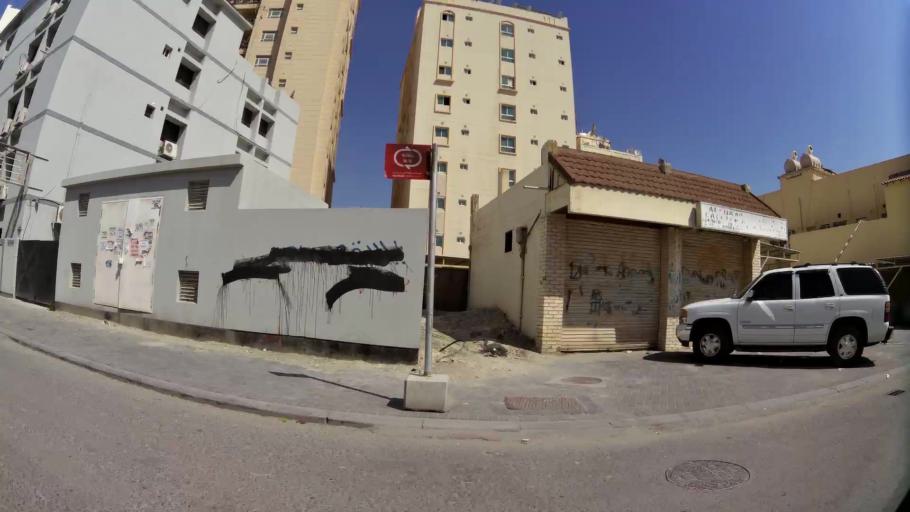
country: BH
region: Manama
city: Manama
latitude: 26.2123
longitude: 50.5997
